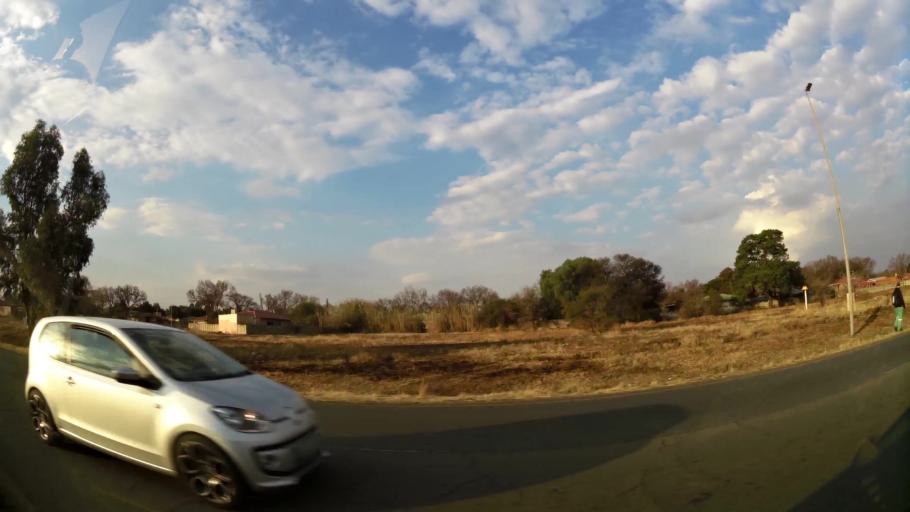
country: ZA
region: Gauteng
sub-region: Sedibeng District Municipality
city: Vanderbijlpark
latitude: -26.7024
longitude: 27.8113
